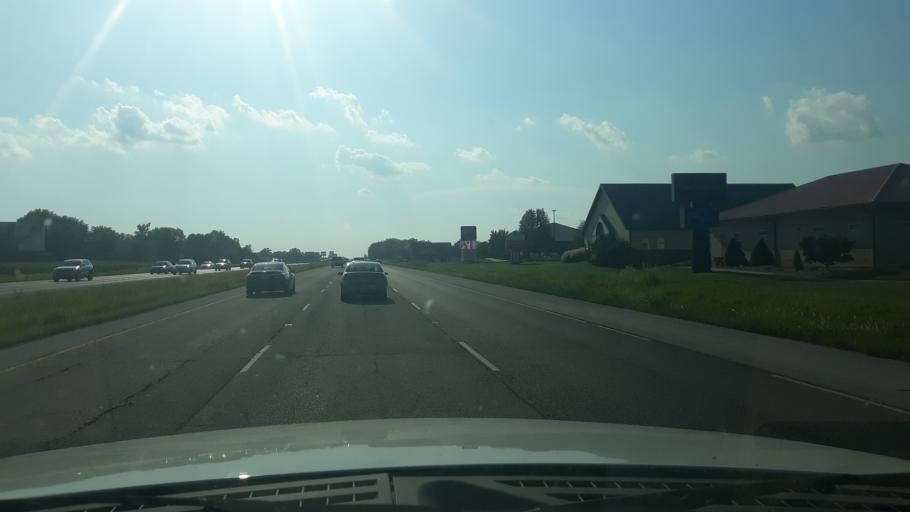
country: US
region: Illinois
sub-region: Williamson County
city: Energy
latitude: 37.7452
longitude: -89.0262
